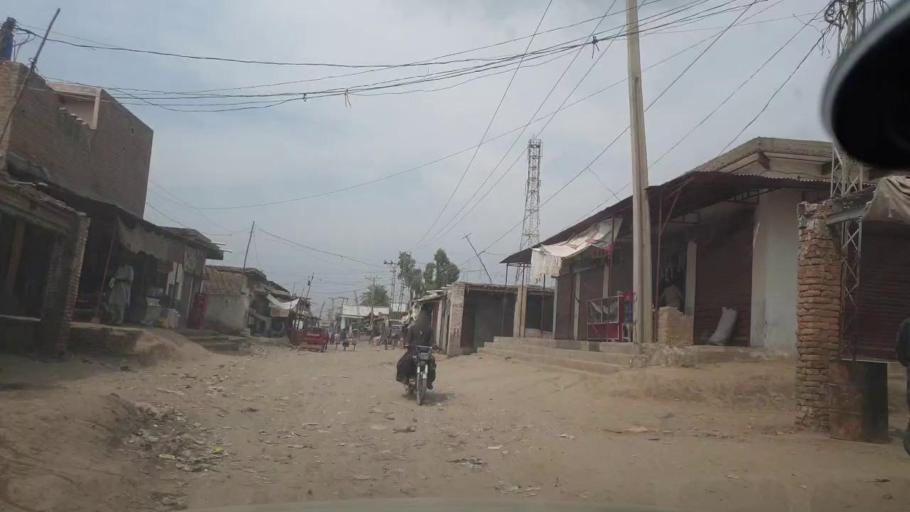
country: PK
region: Sindh
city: Jacobabad
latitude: 28.2684
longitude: 68.4378
